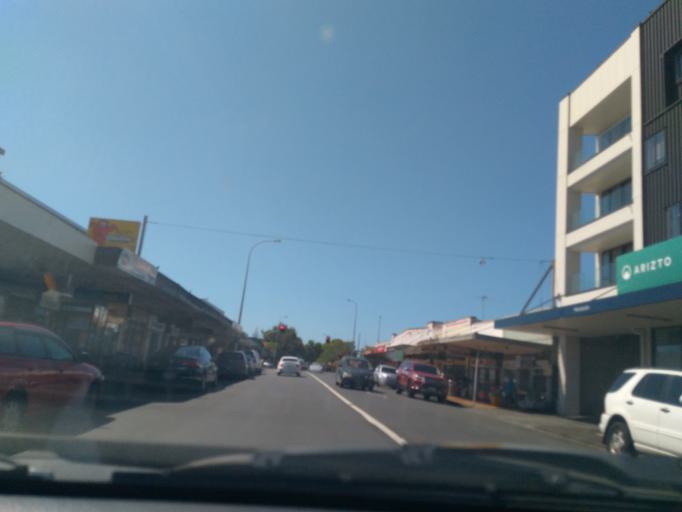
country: NZ
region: Auckland
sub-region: Auckland
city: Rosebank
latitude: -36.8954
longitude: 174.6968
